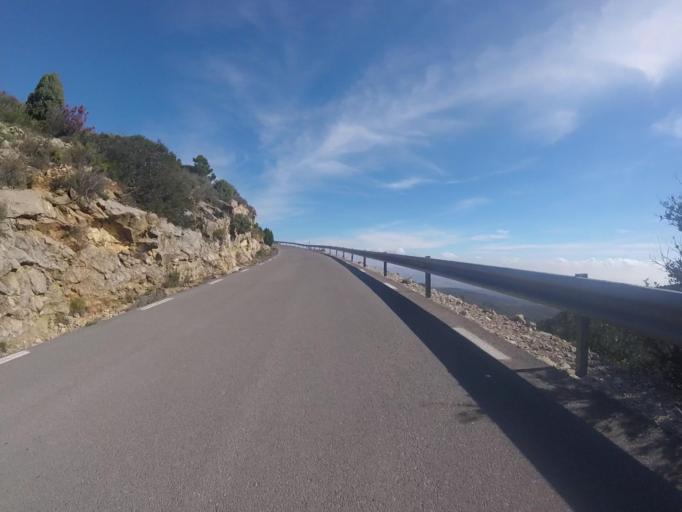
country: ES
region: Valencia
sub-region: Provincia de Castello
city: Sarratella
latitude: 40.2882
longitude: 0.0350
